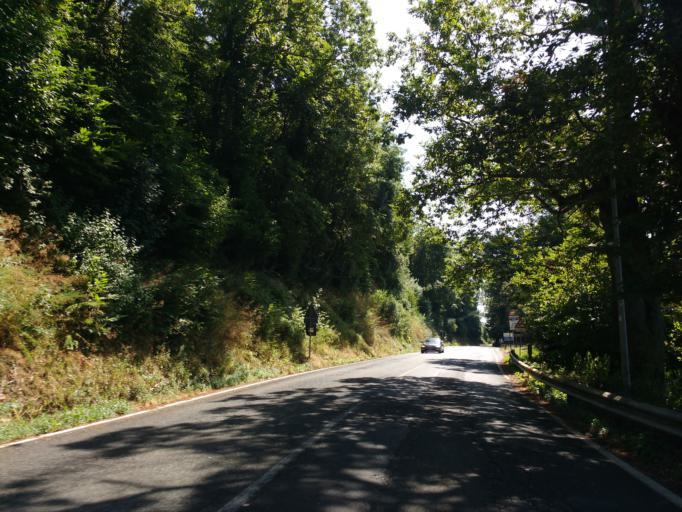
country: IT
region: Latium
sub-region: Citta metropolitana di Roma Capitale
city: Rocca di Papa
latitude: 41.7508
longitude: 12.6994
